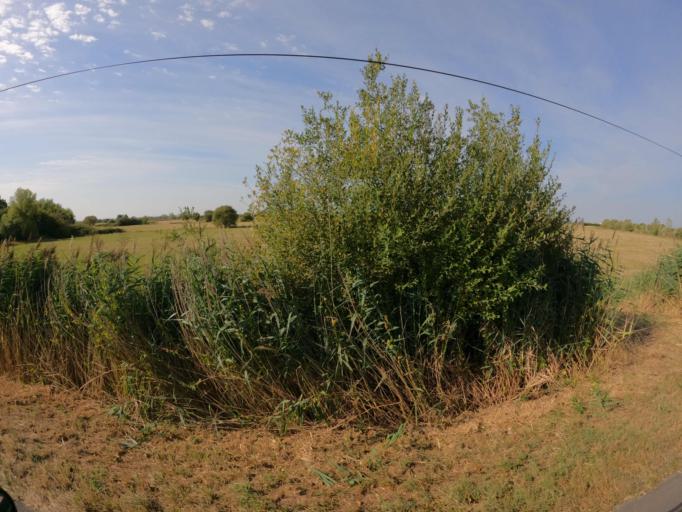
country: FR
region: Pays de la Loire
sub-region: Departement de la Vendee
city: Soullans
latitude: 46.8086
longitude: -1.9273
